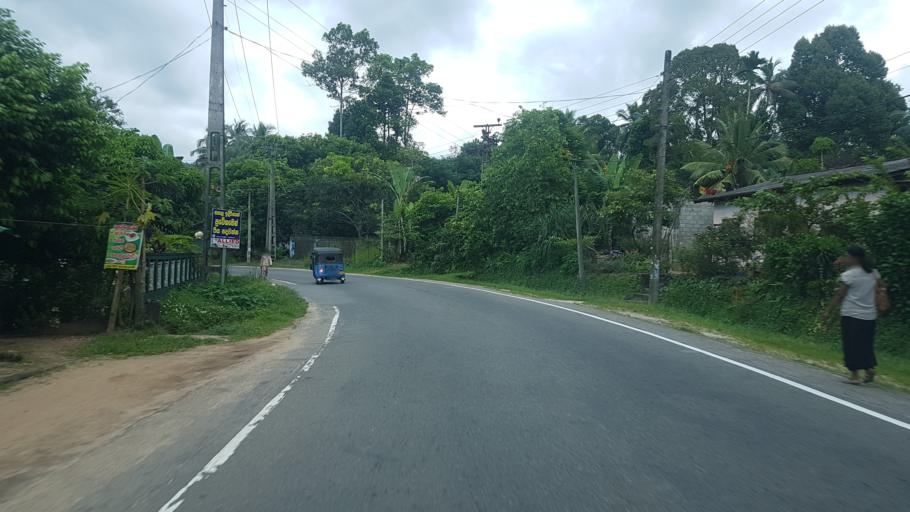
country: LK
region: Western
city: Hanwella Ihala
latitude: 7.0226
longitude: 80.2638
